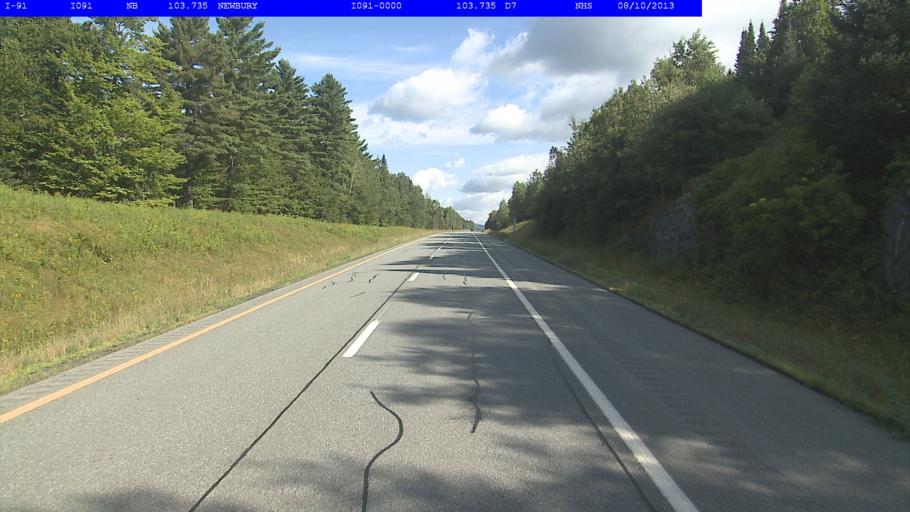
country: US
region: New Hampshire
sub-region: Grafton County
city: Haverhill
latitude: 44.0672
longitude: -72.1098
